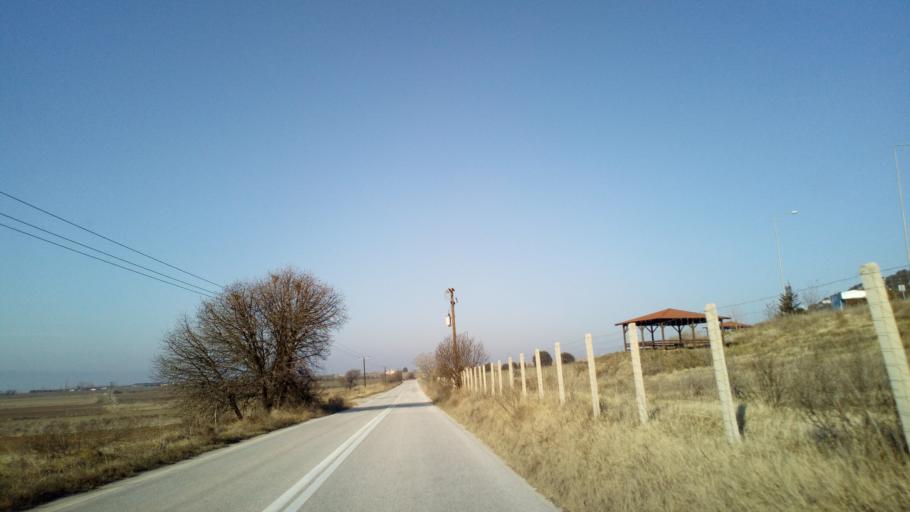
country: GR
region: Central Macedonia
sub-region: Nomos Thessalonikis
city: Kolchikon
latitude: 40.7065
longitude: 23.1896
